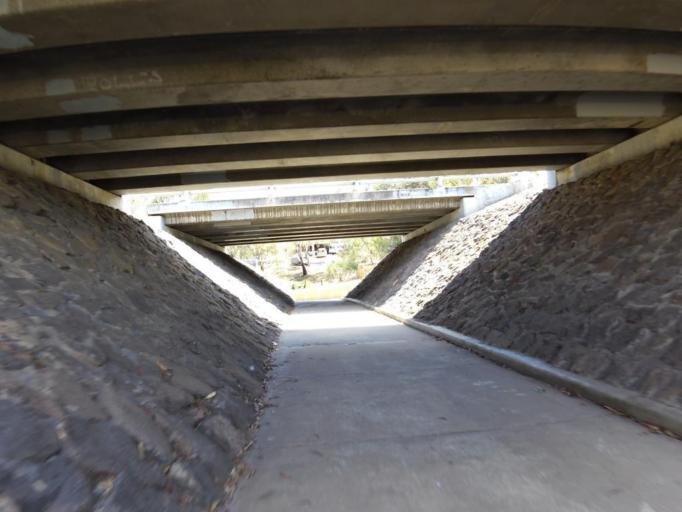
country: AU
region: Victoria
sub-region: Hume
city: Roxburgh Park
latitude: -37.6356
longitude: 144.9229
